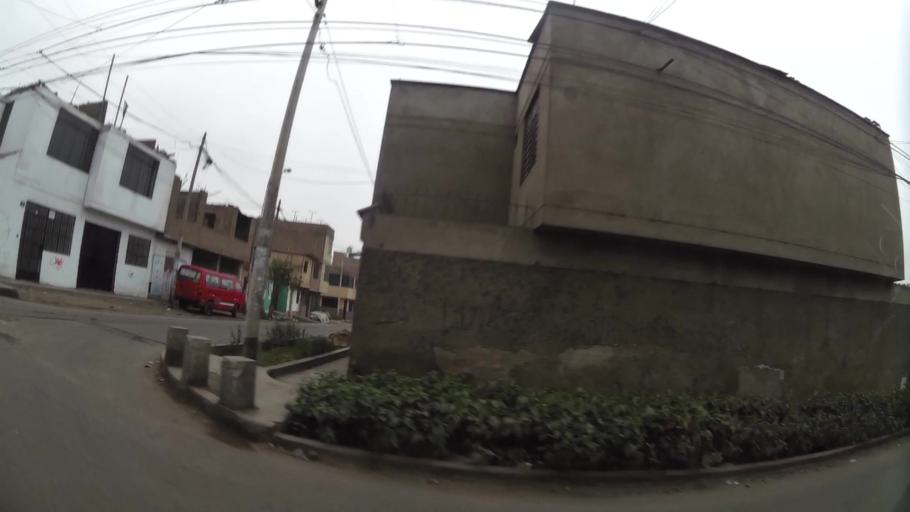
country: PE
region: Lima
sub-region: Lima
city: Surco
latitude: -12.1498
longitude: -76.9729
